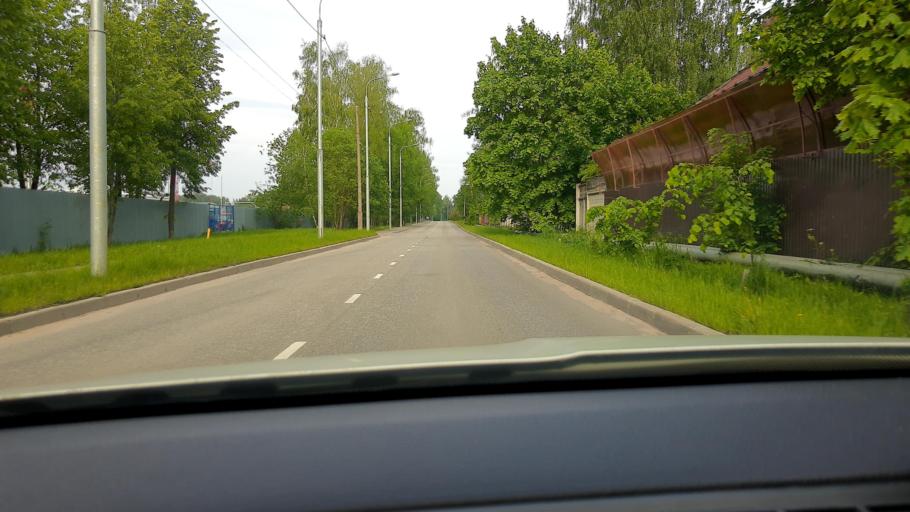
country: RU
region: Moskovskaya
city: Vatutinki
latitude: 55.5095
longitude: 37.3720
